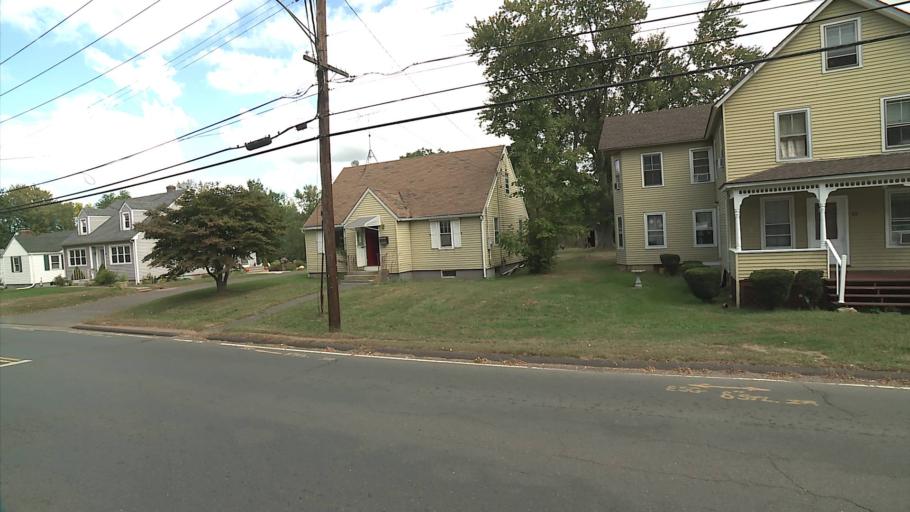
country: US
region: Connecticut
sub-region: Middlesex County
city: Middletown
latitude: 41.5530
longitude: -72.6727
